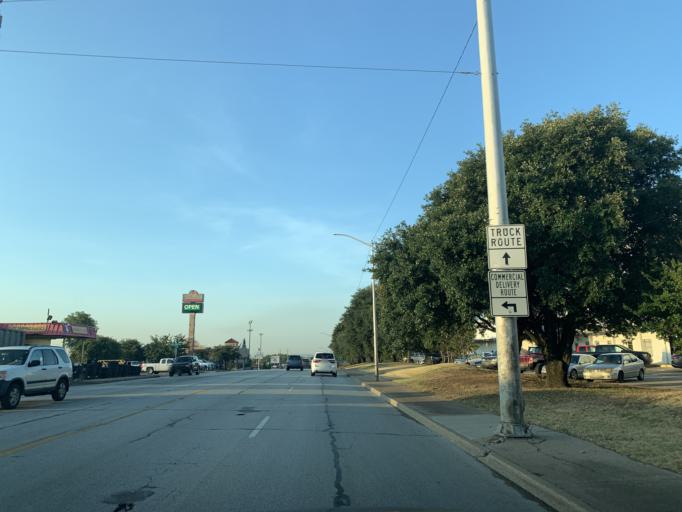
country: US
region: Texas
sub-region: Tarrant County
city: Blue Mound
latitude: 32.8147
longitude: -97.3515
